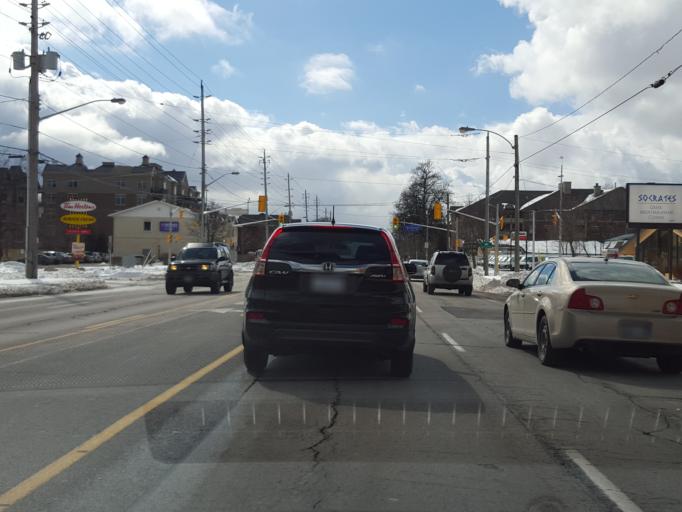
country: CA
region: Ontario
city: Burlington
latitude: 43.3179
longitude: -79.8379
